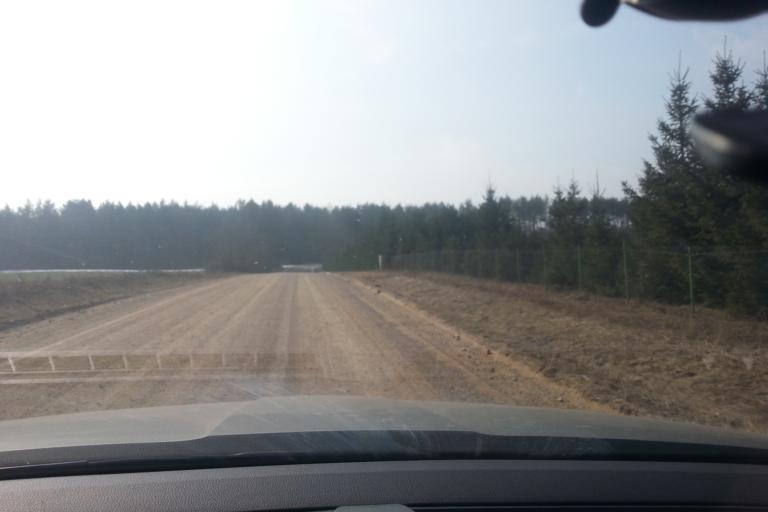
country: LT
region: Vilnius County
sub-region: Trakai
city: Rudiskes
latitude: 54.5143
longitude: 24.9361
